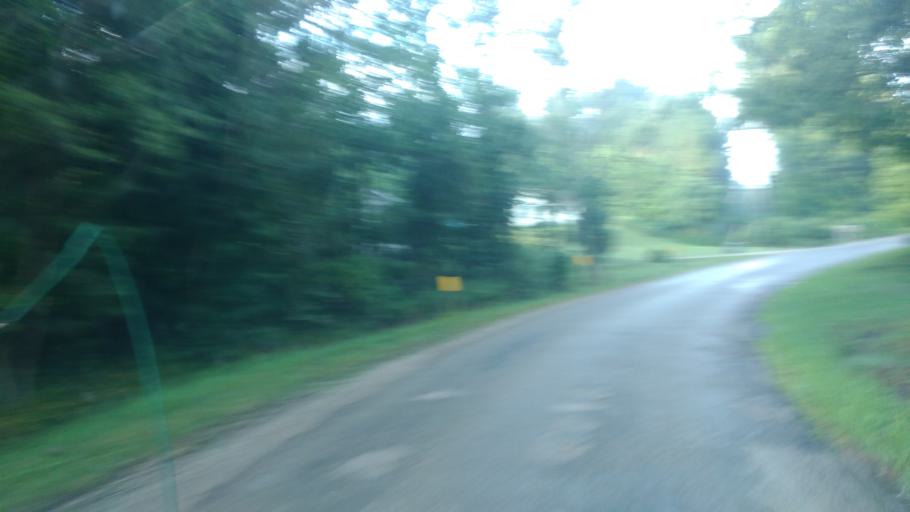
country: US
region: Ohio
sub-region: Guernsey County
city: Byesville
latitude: 39.9960
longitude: -81.5448
